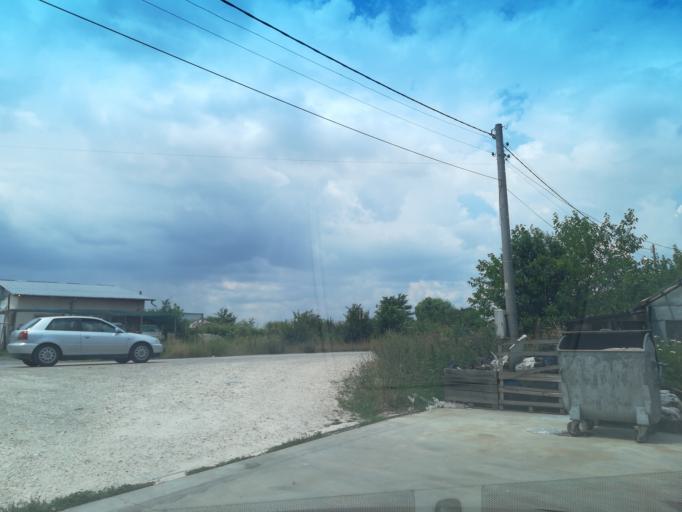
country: BG
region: Stara Zagora
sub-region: Obshtina Chirpan
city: Chirpan
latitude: 42.1775
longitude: 25.2075
